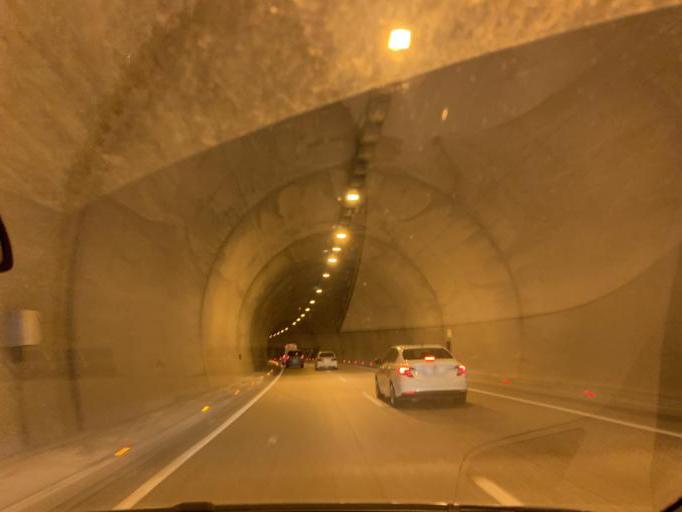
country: TR
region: Bursa
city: Kursunlu
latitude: 40.0057
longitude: 29.6524
